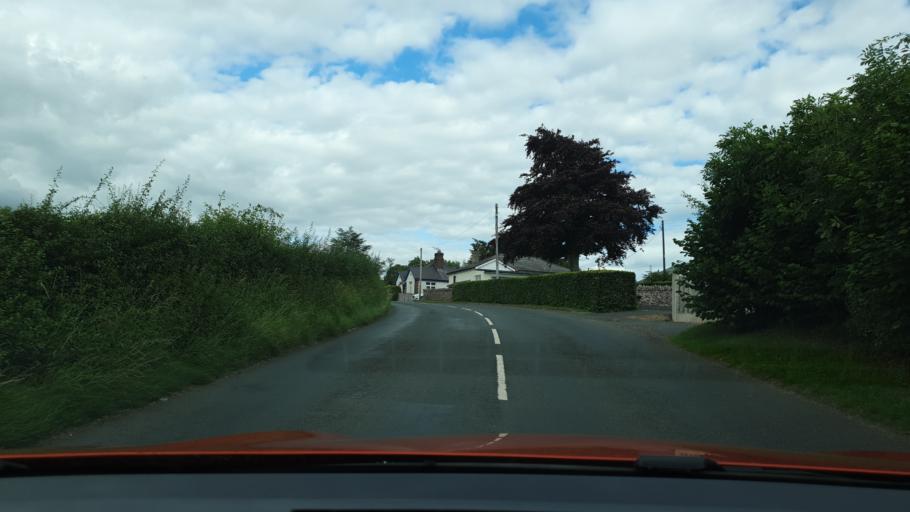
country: GB
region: England
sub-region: Cumbria
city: Penrith
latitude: 54.6293
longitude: -2.7825
